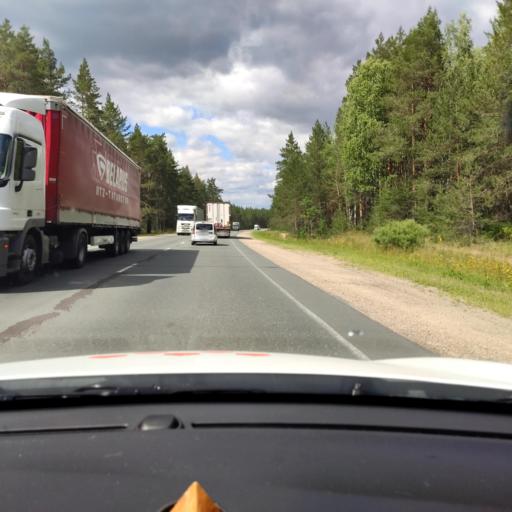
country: RU
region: Mariy-El
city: Krasnogorskiy
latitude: 56.0964
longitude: 48.3455
